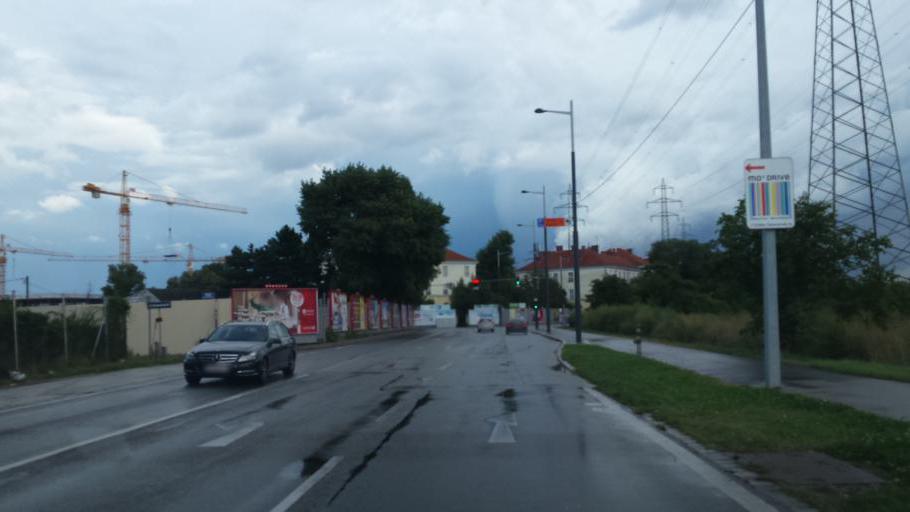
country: AT
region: Lower Austria
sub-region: Politischer Bezirk Wien-Umgebung
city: Schwechat
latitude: 48.1677
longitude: 16.4679
